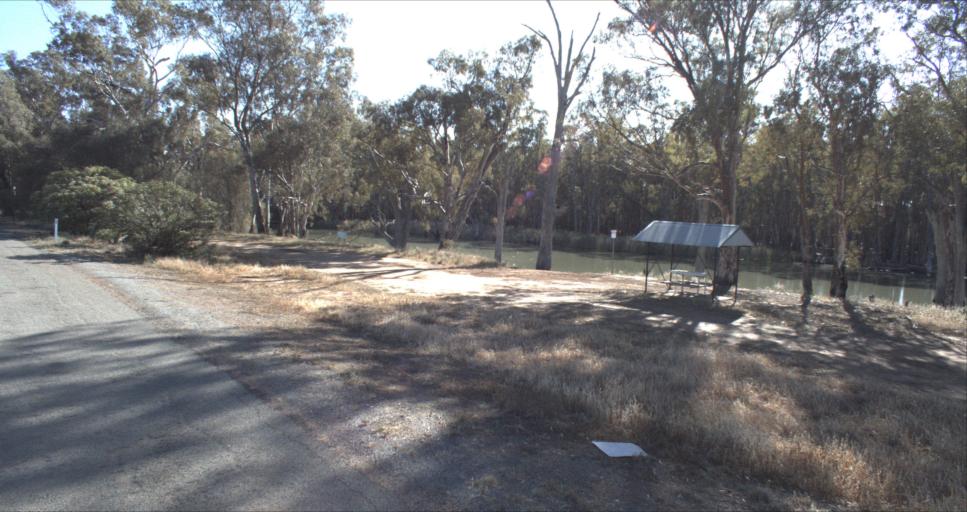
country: AU
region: New South Wales
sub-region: Leeton
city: Leeton
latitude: -34.6122
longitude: 146.2598
